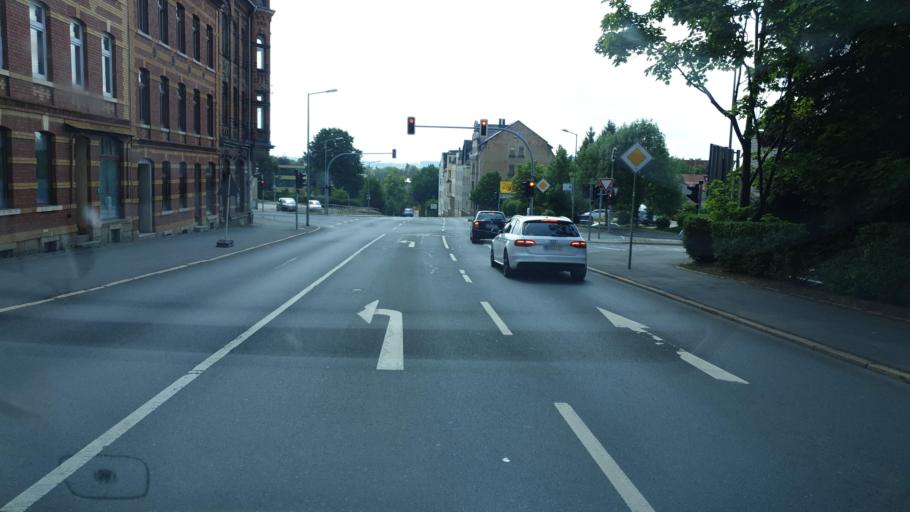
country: DE
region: Saxony
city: Reichenbach/Vogtland
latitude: 50.6269
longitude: 12.2883
